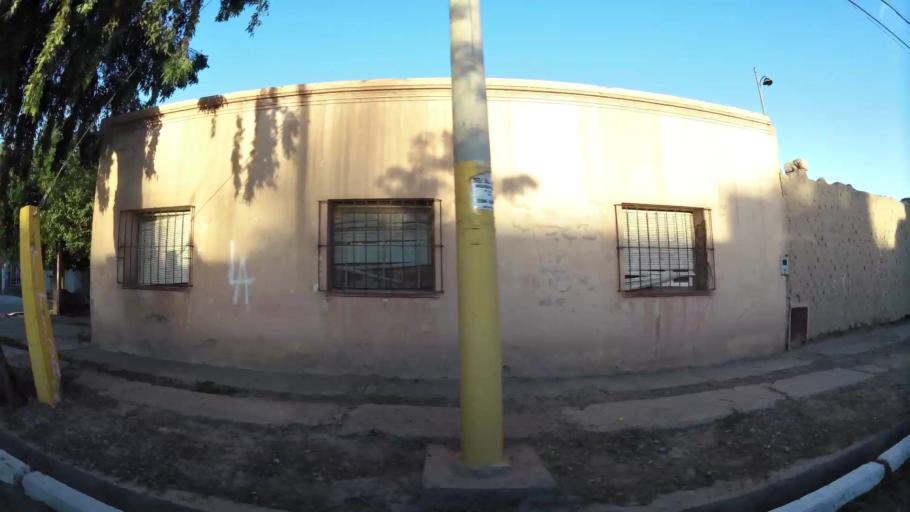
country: AR
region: San Juan
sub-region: Departamento de Santa Lucia
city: Santa Lucia
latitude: -31.5234
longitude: -68.5075
